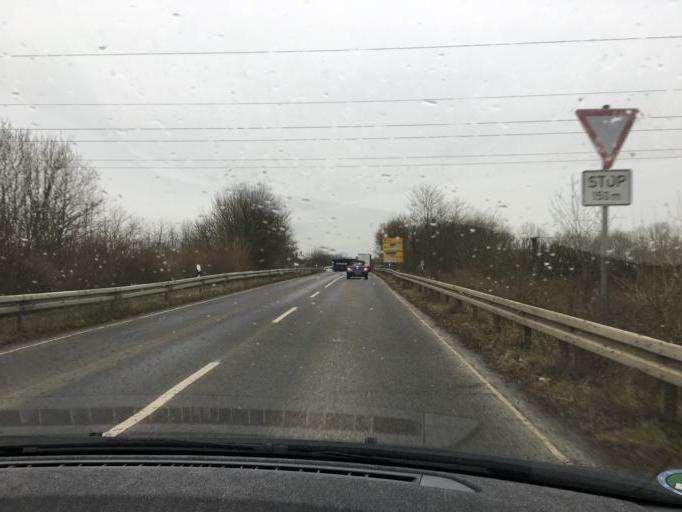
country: DE
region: North Rhine-Westphalia
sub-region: Regierungsbezirk Koln
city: Bergheim
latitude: 50.9367
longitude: 6.6161
